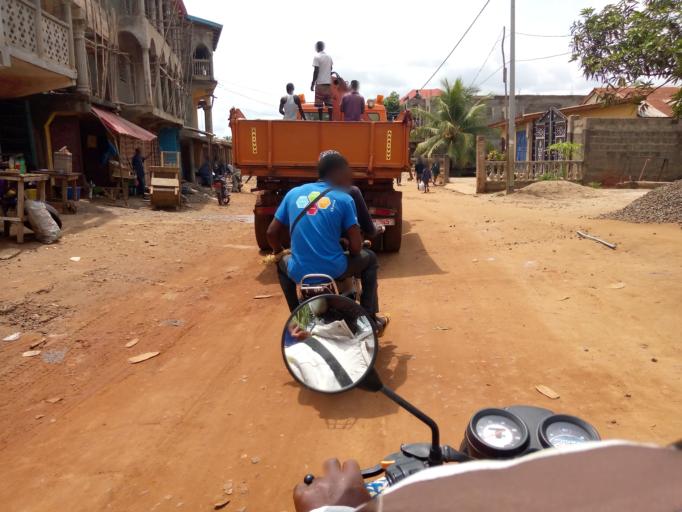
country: SL
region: Western Area
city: Waterloo
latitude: 8.3593
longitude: -13.0769
